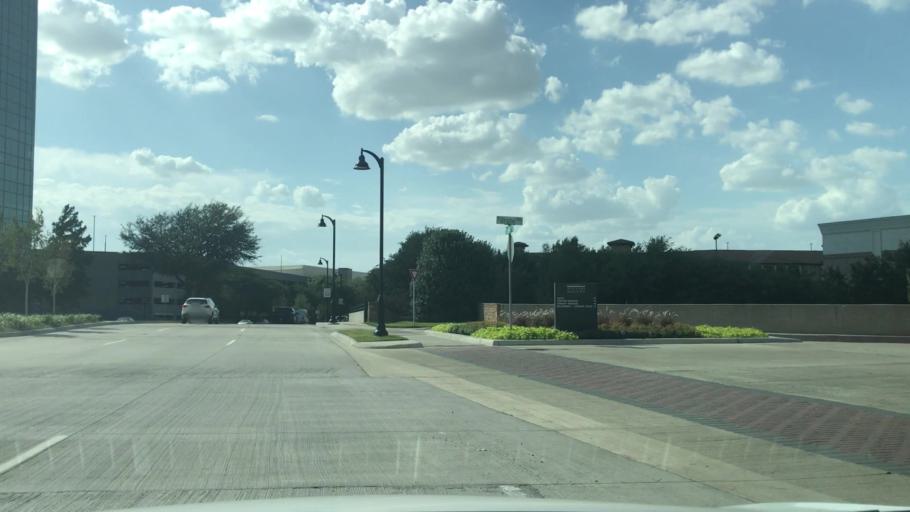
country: US
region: Texas
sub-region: Dallas County
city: Irving
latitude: 32.8707
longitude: -96.9416
